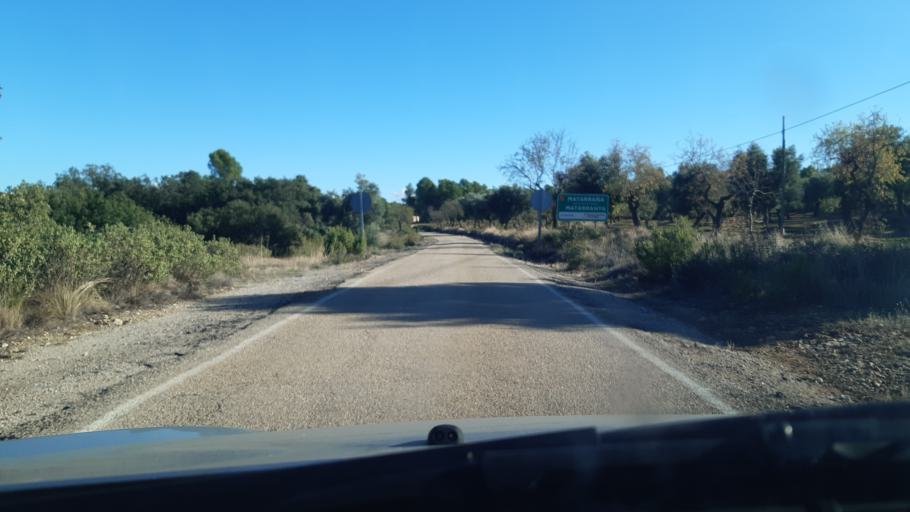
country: ES
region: Aragon
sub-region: Provincia de Teruel
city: Fornoles
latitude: 40.9137
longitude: -0.0195
